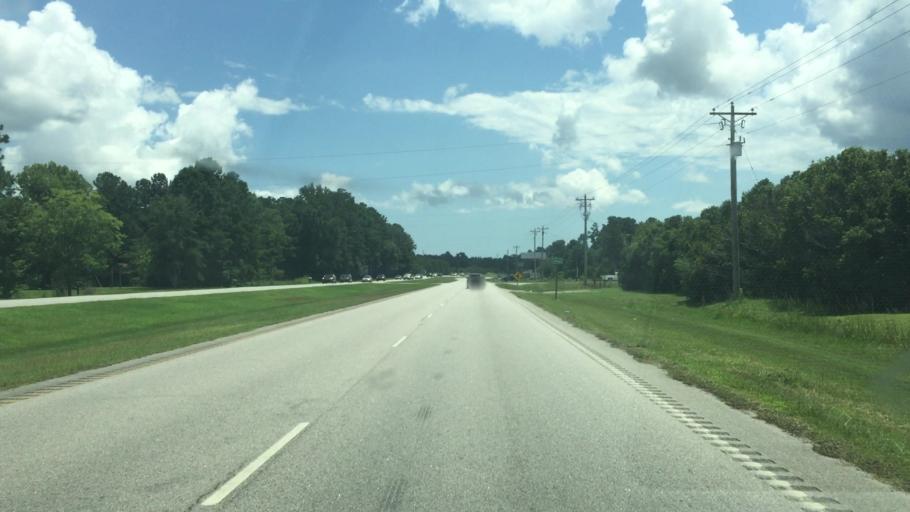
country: US
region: South Carolina
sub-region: Horry County
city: Little River
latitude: 33.9588
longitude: -78.7371
